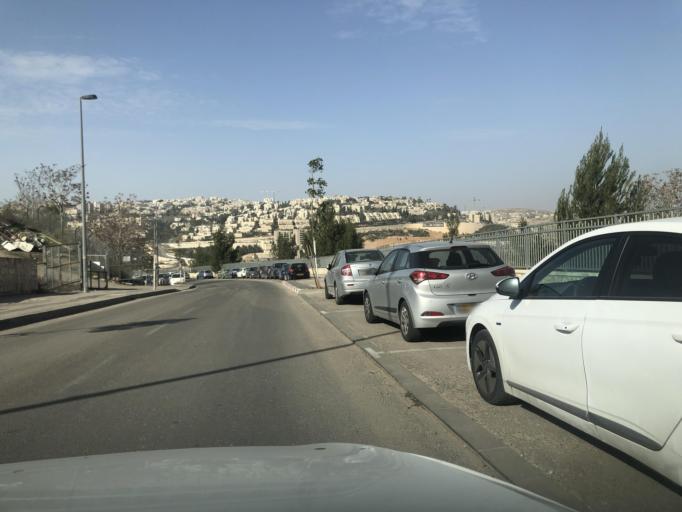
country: IL
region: Jerusalem
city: West Jerusalem
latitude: 31.8048
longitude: 35.2101
